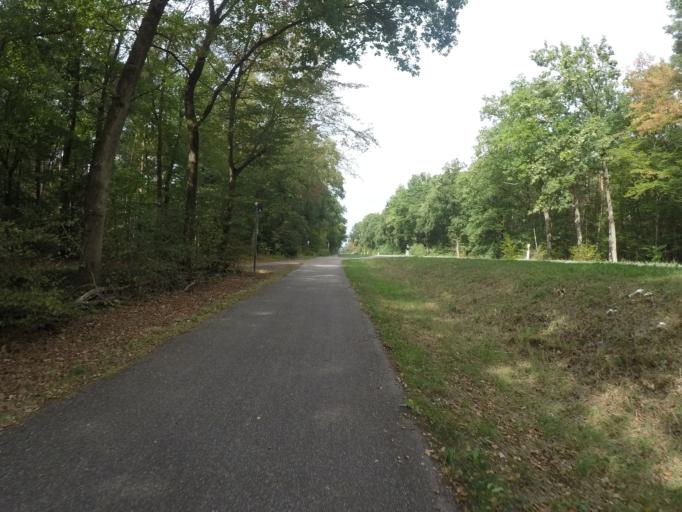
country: DE
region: Rheinland-Pfalz
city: Hanhofen
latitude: 49.3530
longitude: 8.3438
